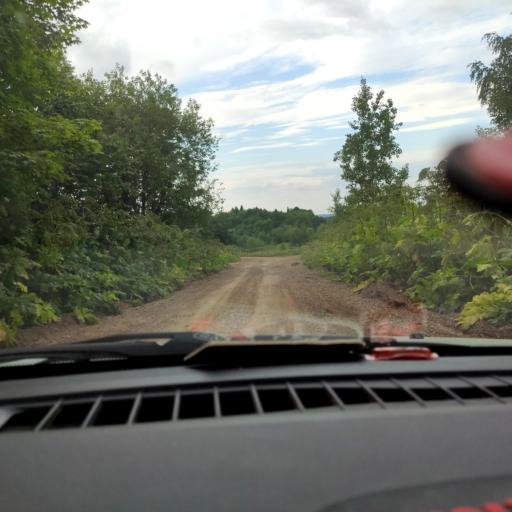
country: RU
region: Perm
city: Kultayevo
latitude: 57.8195
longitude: 55.9997
